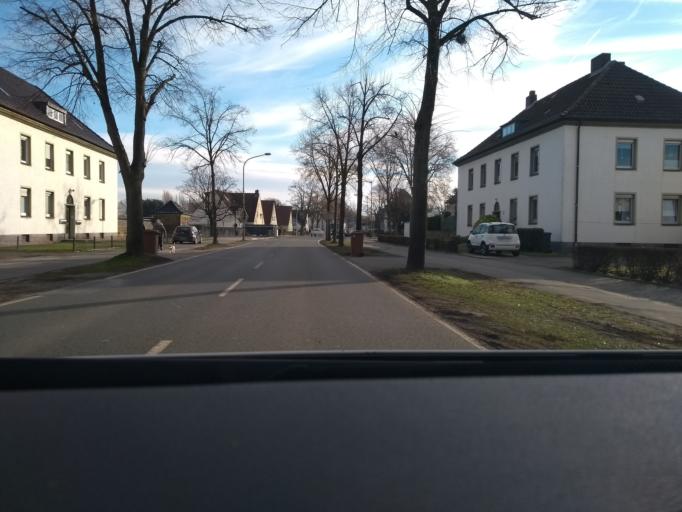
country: DE
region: North Rhine-Westphalia
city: Lunen
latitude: 51.6150
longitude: 7.5016
